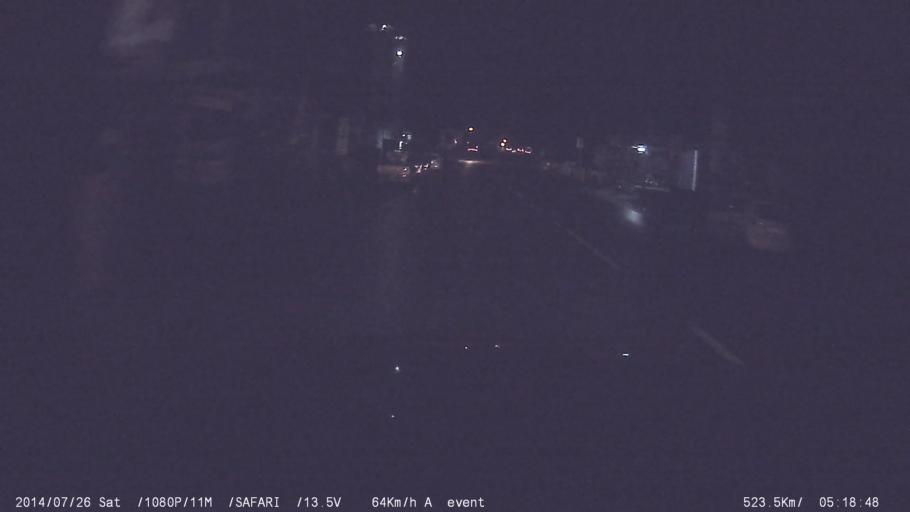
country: IN
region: Kerala
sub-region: Ernakulam
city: Muvattupula
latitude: 10.0053
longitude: 76.5706
